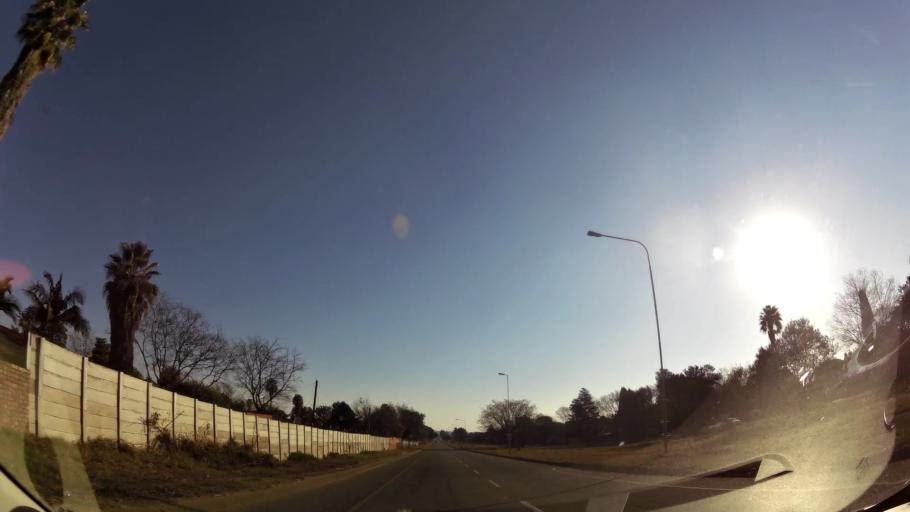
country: ZA
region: Gauteng
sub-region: City of Tshwane Metropolitan Municipality
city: Centurion
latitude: -25.8690
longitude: 28.1458
